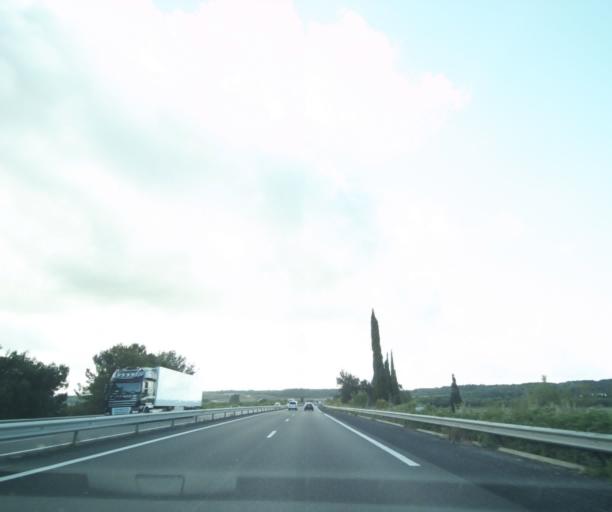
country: FR
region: Languedoc-Roussillon
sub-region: Departement du Gard
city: Bellegarde
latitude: 43.7310
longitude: 4.4821
